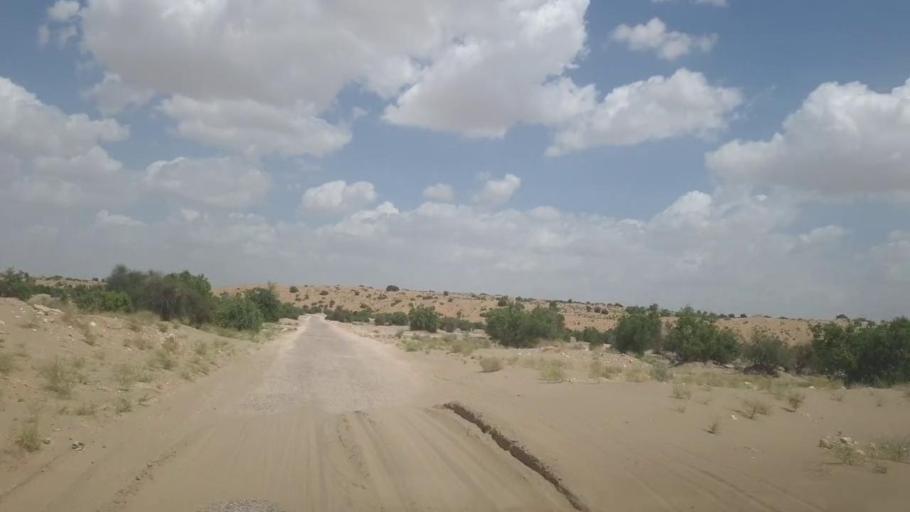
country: PK
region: Sindh
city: Kot Diji
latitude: 27.2529
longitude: 69.1573
